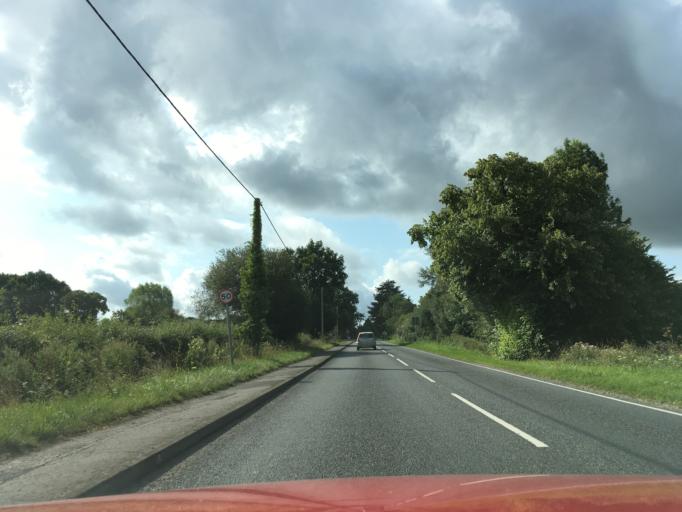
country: GB
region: England
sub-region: Hampshire
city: Bishops Waltham
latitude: 50.9407
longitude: -1.2023
